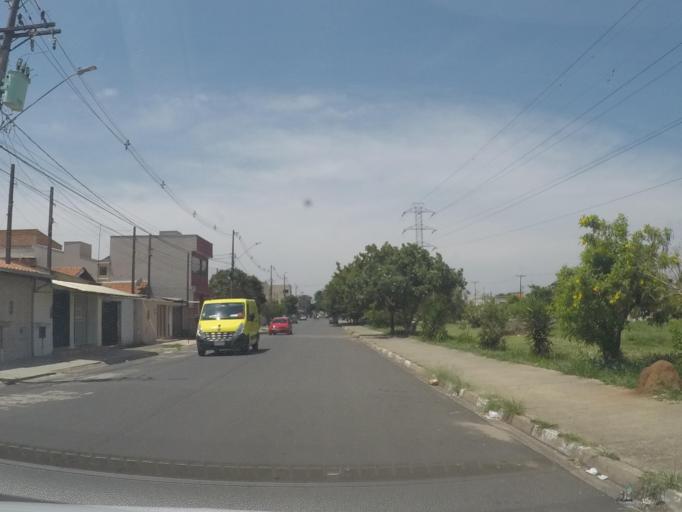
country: BR
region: Sao Paulo
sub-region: Hortolandia
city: Hortolandia
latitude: -22.8526
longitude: -47.1946
